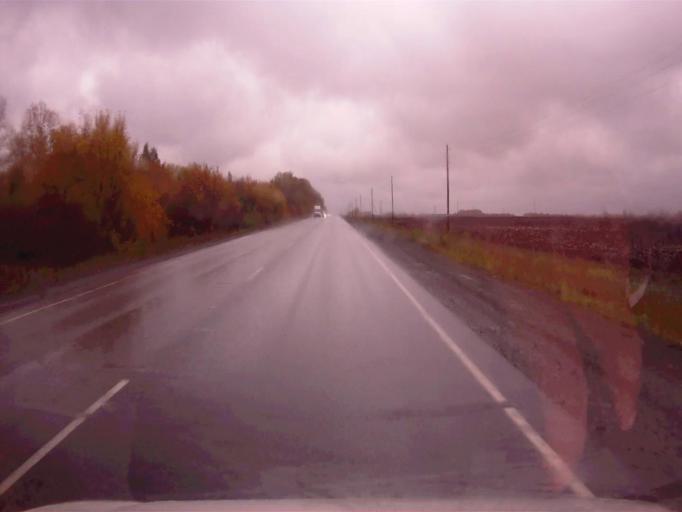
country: RU
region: Chelyabinsk
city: Argayash
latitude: 55.4284
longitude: 60.9960
